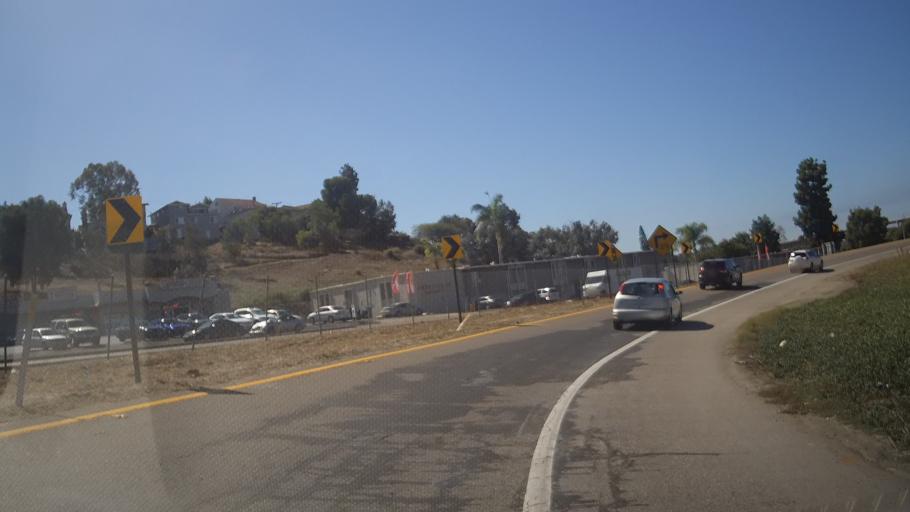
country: US
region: California
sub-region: San Diego County
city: Spring Valley
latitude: 32.7521
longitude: -117.0110
